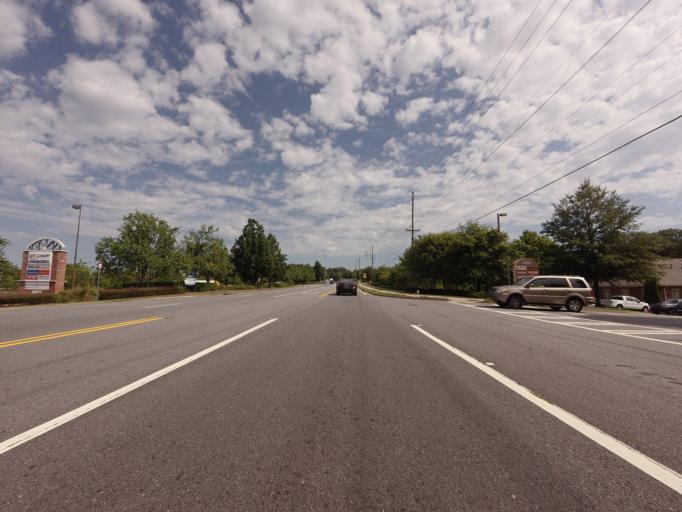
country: US
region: Georgia
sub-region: Fulton County
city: Johns Creek
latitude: 34.0449
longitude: -84.1762
